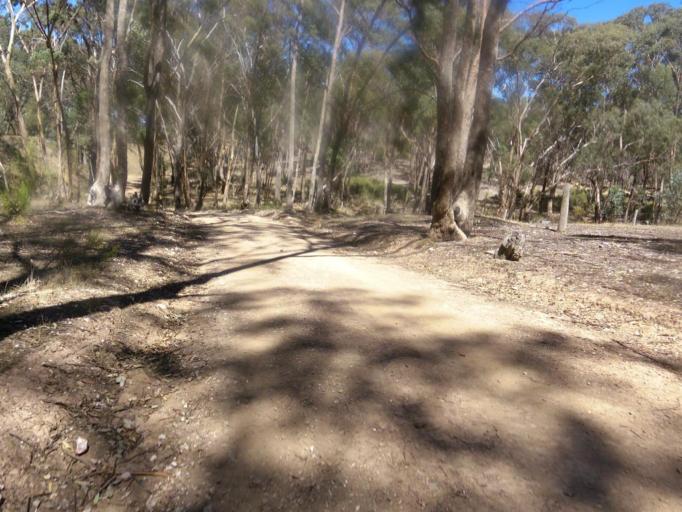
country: AU
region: Victoria
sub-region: Mount Alexander
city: Castlemaine
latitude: -37.0613
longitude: 144.1921
